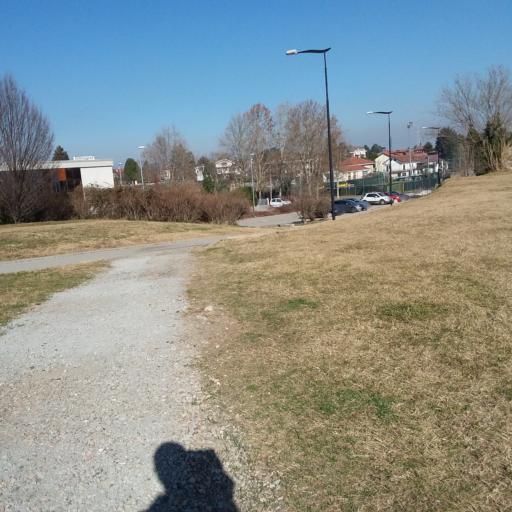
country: IT
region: Piedmont
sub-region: Provincia di Torino
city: Rivoli
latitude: 45.0735
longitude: 7.5355
